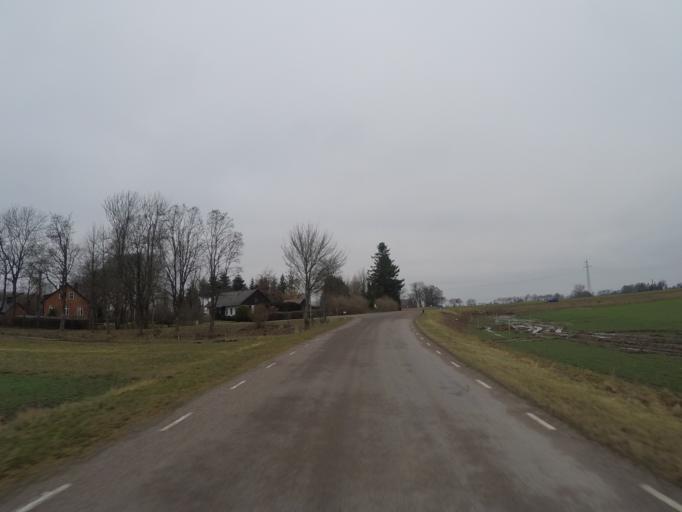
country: SE
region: Skane
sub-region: Hoors Kommun
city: Loberod
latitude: 55.7678
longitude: 13.4459
